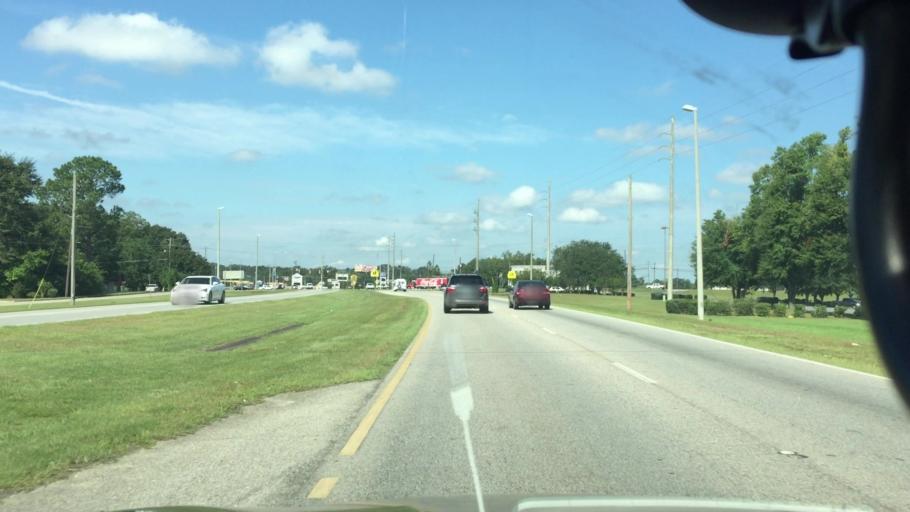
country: US
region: Alabama
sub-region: Coffee County
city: Enterprise
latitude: 31.3347
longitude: -85.8506
